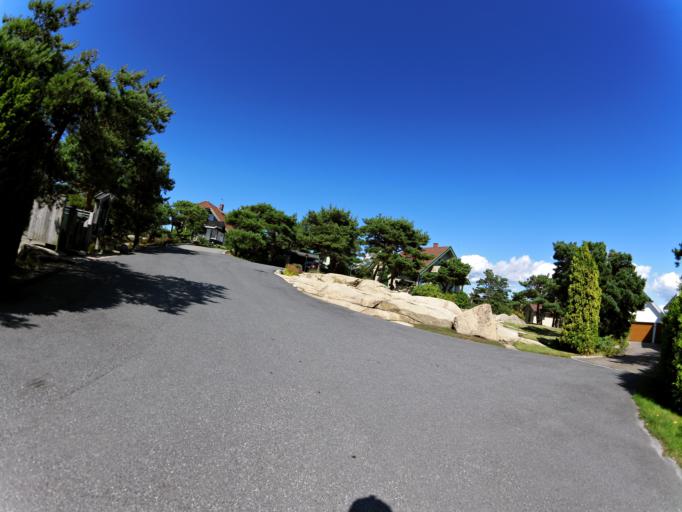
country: NO
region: Ostfold
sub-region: Fredrikstad
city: Fredrikstad
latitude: 59.1735
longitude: 10.8523
